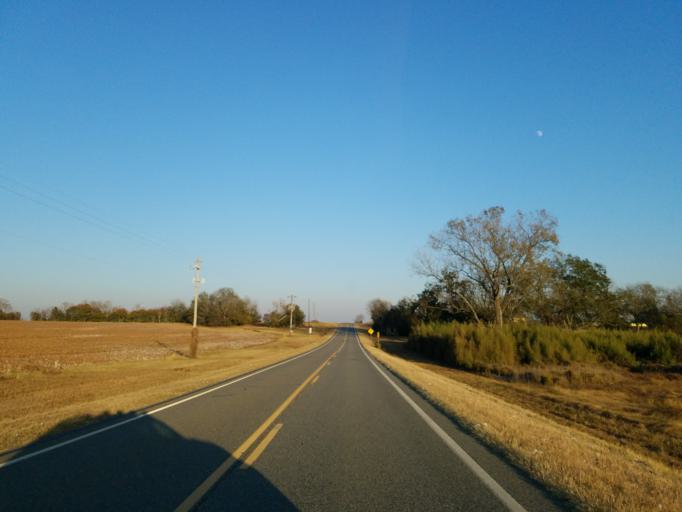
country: US
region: Georgia
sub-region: Turner County
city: Ashburn
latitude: 31.8597
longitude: -83.6037
